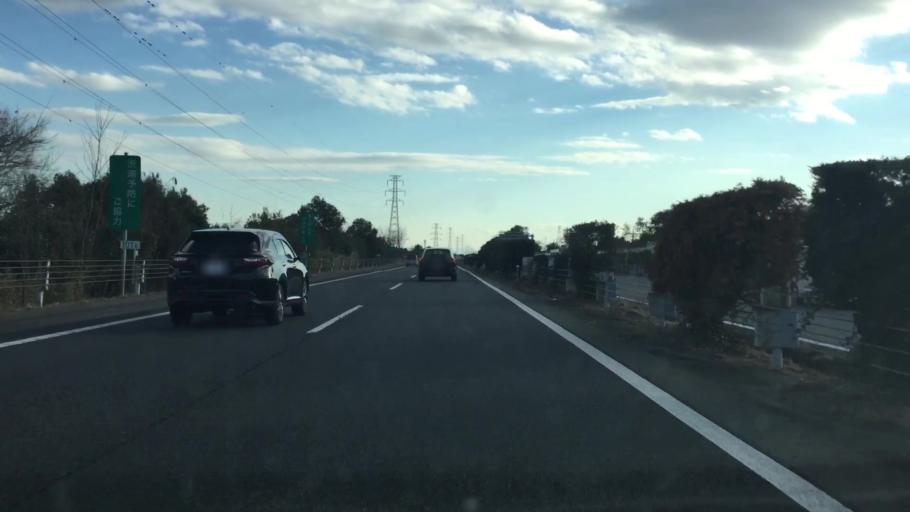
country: JP
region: Gunma
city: Shibukawa
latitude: 36.4584
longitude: 139.0128
